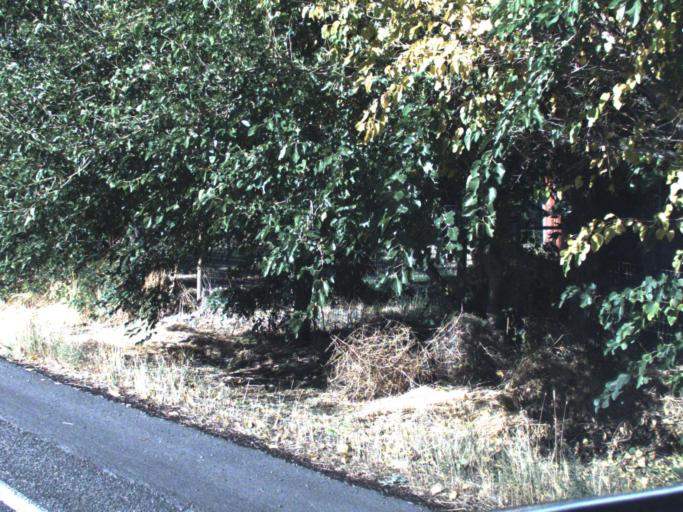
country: US
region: Washington
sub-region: Benton County
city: Finley
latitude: 46.1514
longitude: -119.0261
